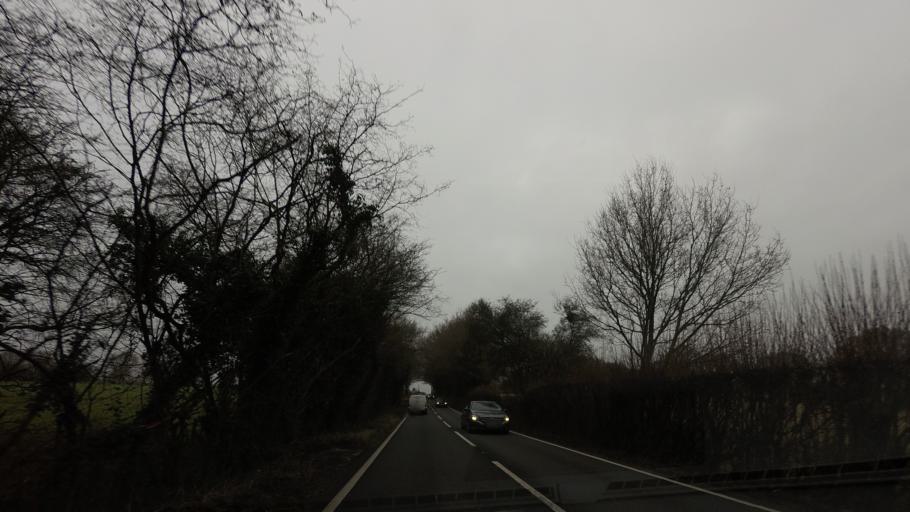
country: GB
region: England
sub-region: East Sussex
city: Saint Leonards-on-Sea
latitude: 50.9066
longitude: 0.5482
